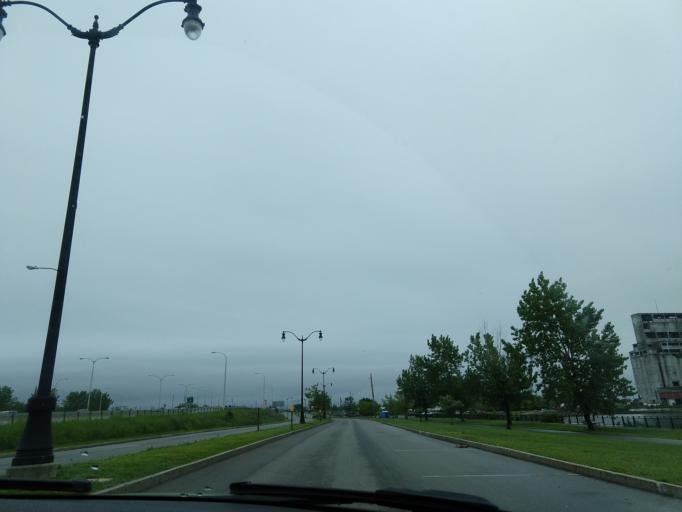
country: US
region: New York
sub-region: Erie County
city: Lackawanna
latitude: 42.8427
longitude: -78.8593
